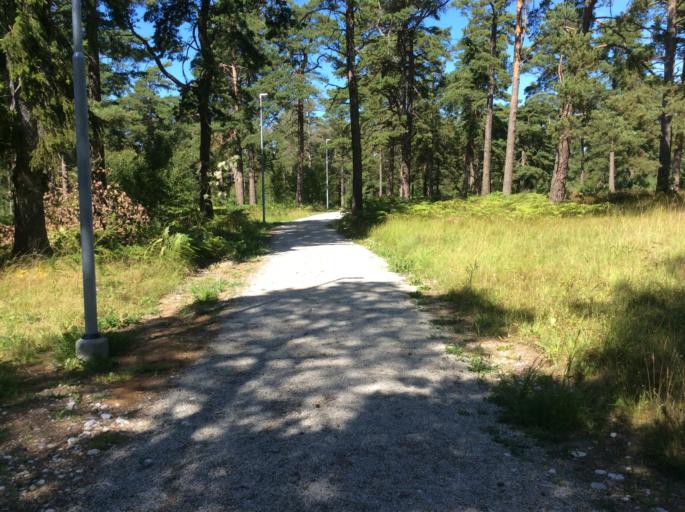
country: SE
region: Gotland
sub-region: Gotland
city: Vibble
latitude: 57.6015
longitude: 18.2782
